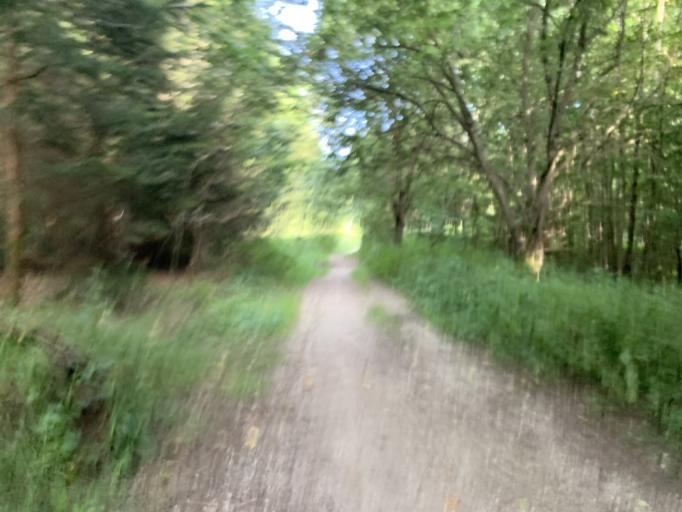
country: DE
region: Bavaria
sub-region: Upper Bavaria
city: Freising
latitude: 48.4203
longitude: 11.7403
